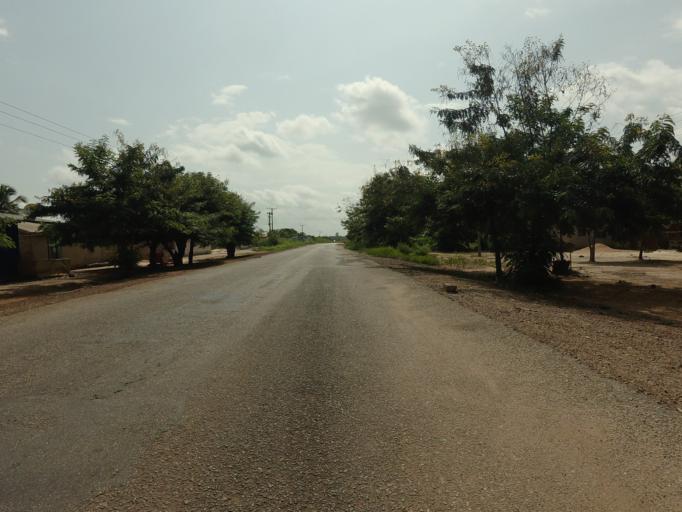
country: TG
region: Maritime
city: Lome
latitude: 6.2562
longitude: 0.9648
